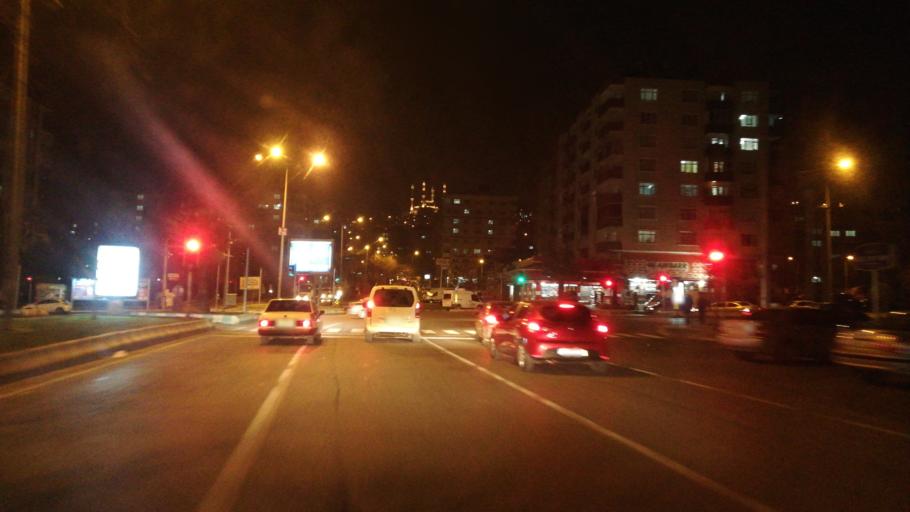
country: TR
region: Kahramanmaras
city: Kahramanmaras
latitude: 37.5777
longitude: 36.9243
